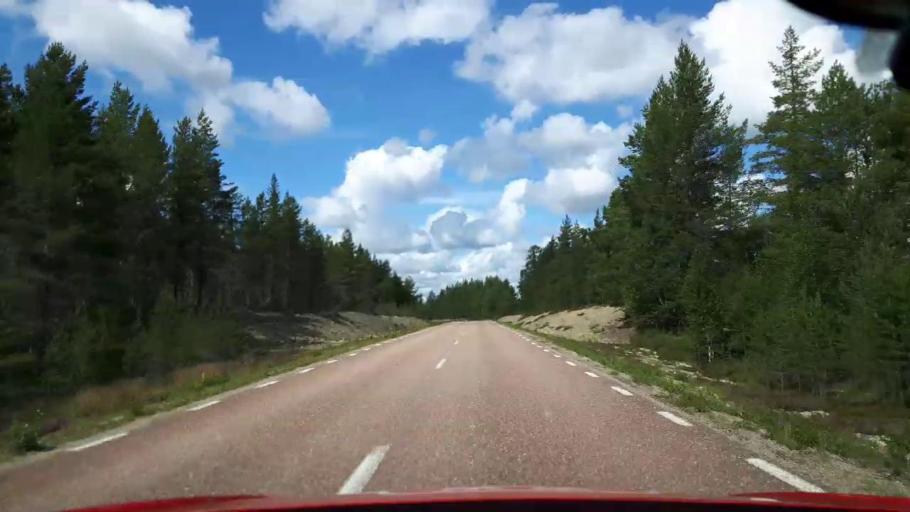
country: SE
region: Dalarna
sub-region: Alvdalens Kommun
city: AElvdalen
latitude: 61.8041
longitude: 13.6560
